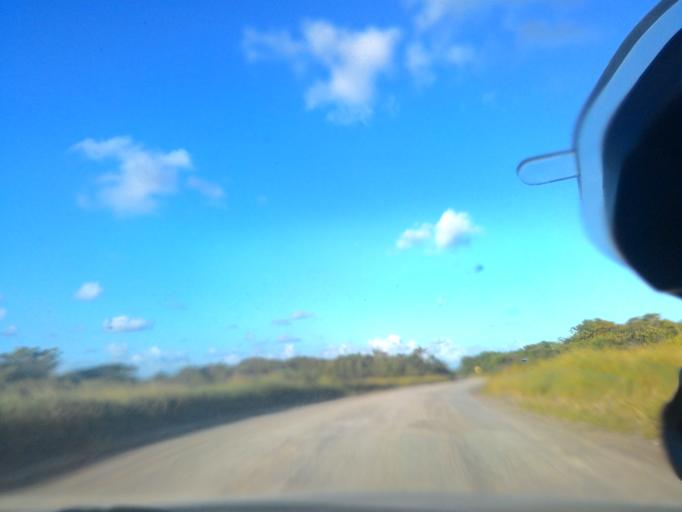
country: BR
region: Sao Paulo
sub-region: Pariquera-Acu
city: Pariquera Acu
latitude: -24.8769
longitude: -47.7329
